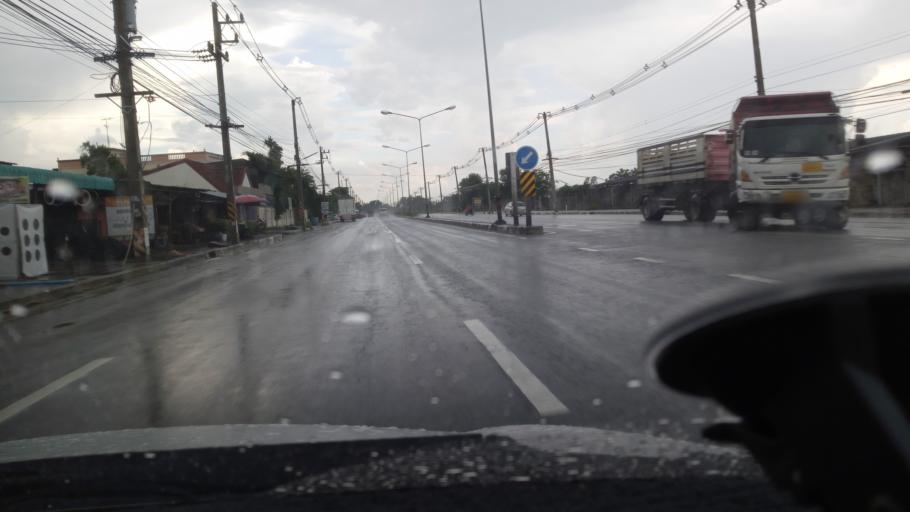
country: TH
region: Chon Buri
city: Phan Thong
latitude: 13.4537
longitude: 101.0967
